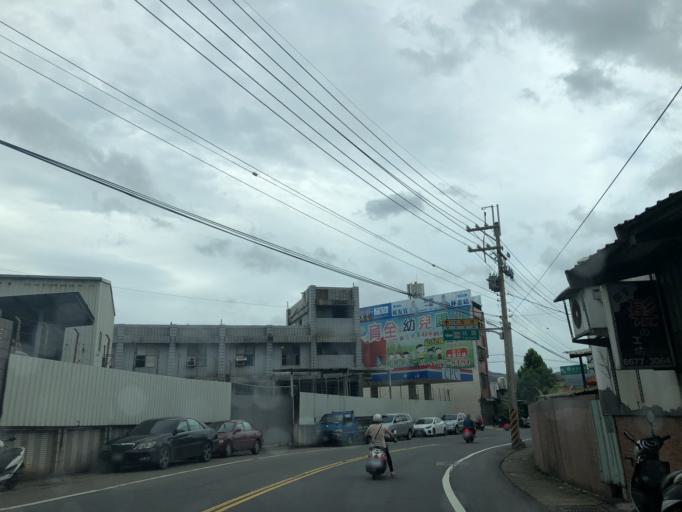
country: TW
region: Taiwan
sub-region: Taoyuan
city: Taoyuan
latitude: 24.9472
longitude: 121.3403
